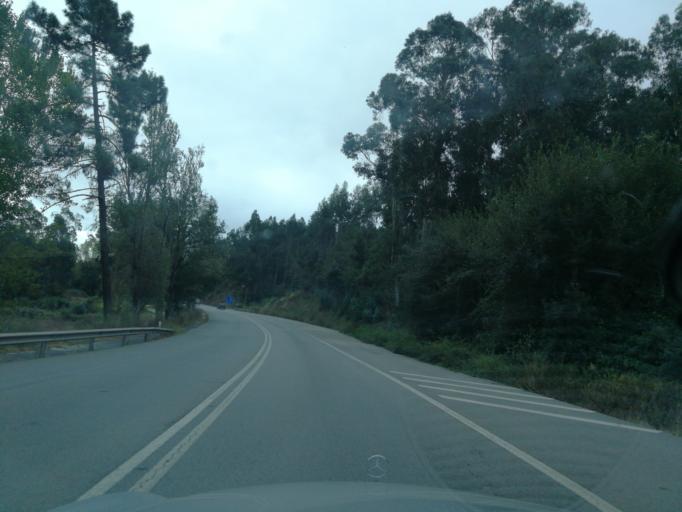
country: PT
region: Aveiro
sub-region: Agueda
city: Valongo
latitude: 40.6319
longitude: -8.4700
